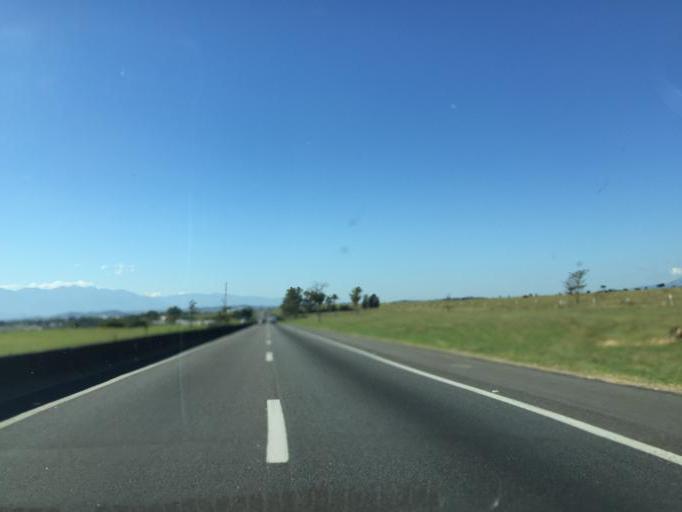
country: BR
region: Sao Paulo
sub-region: Lorena
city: Lorena
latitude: -22.7260
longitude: -45.0703
